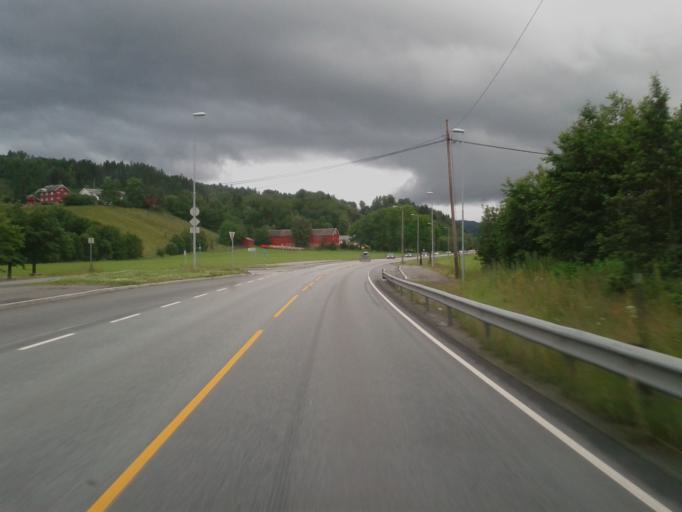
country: NO
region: Sor-Trondelag
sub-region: Melhus
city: Lundamo
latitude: 63.1369
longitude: 10.2534
